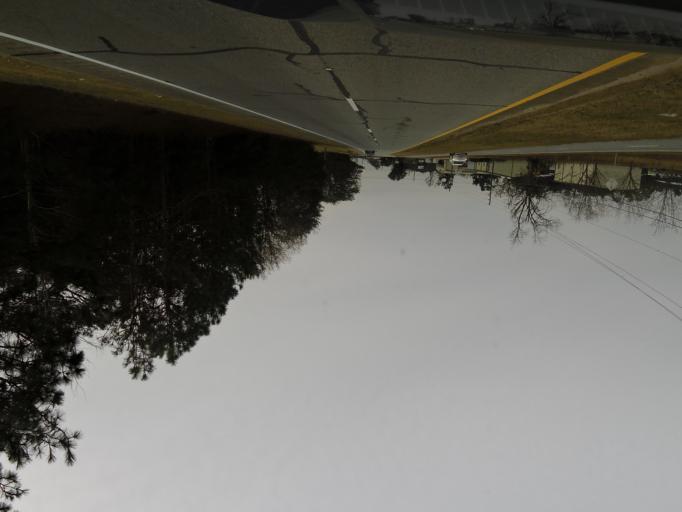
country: US
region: Georgia
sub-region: Decatur County
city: Bainbridge
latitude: 30.9274
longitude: -84.6216
